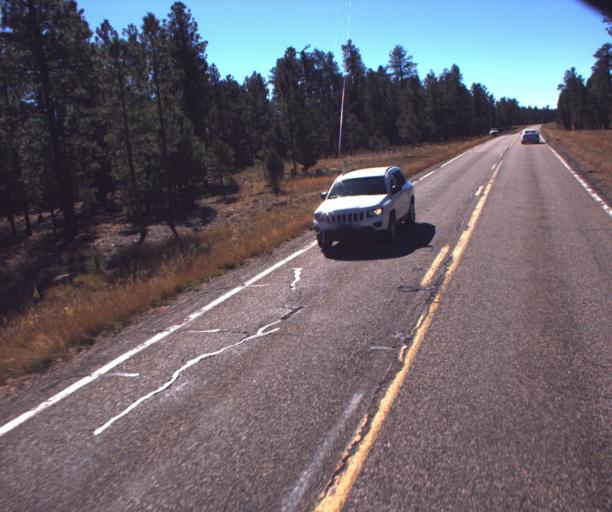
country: US
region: Arizona
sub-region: Coconino County
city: Fredonia
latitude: 36.7259
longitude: -112.2128
